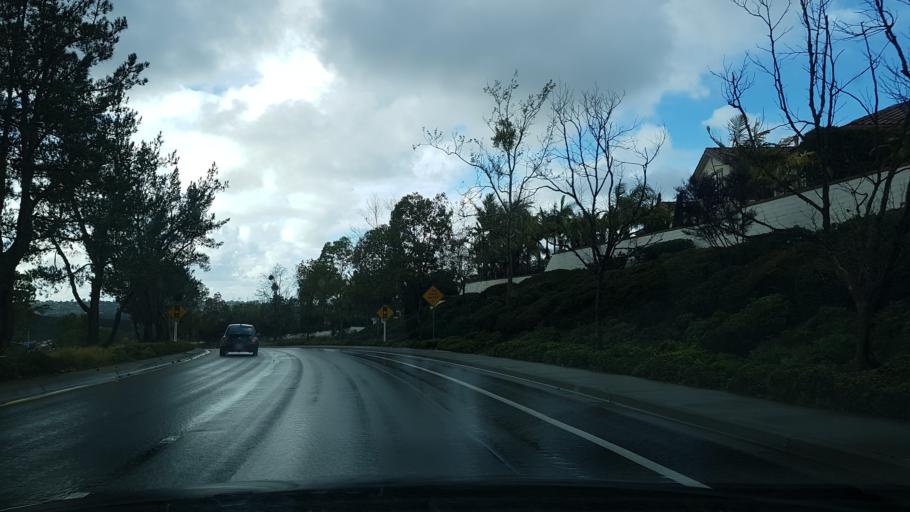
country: US
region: California
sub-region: San Diego County
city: Fairbanks Ranch
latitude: 32.9340
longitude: -117.2035
